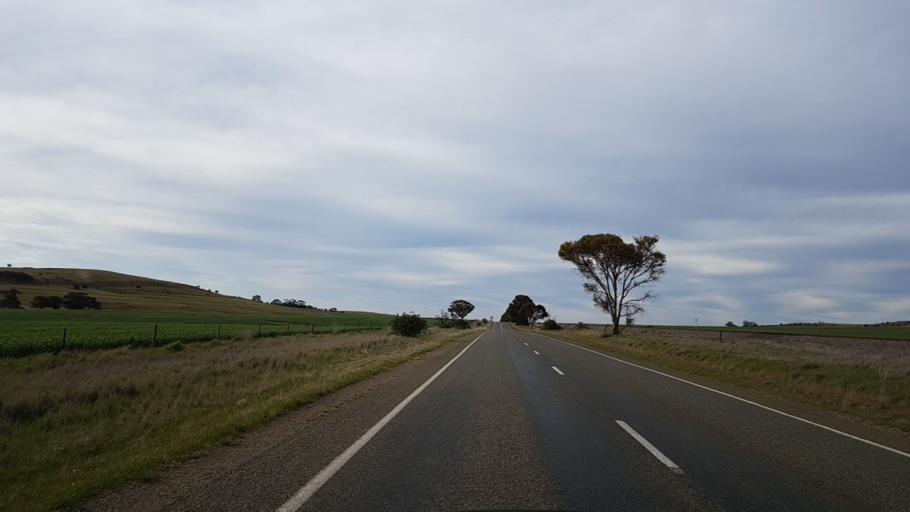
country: AU
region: South Australia
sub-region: Northern Areas
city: Jamestown
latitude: -33.1371
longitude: 138.6169
